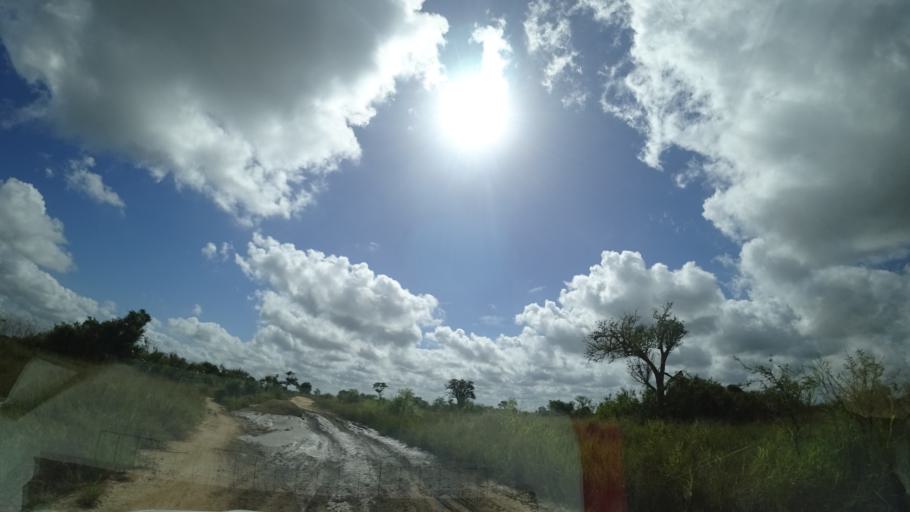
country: MZ
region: Sofala
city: Dondo
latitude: -19.4065
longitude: 34.5663
